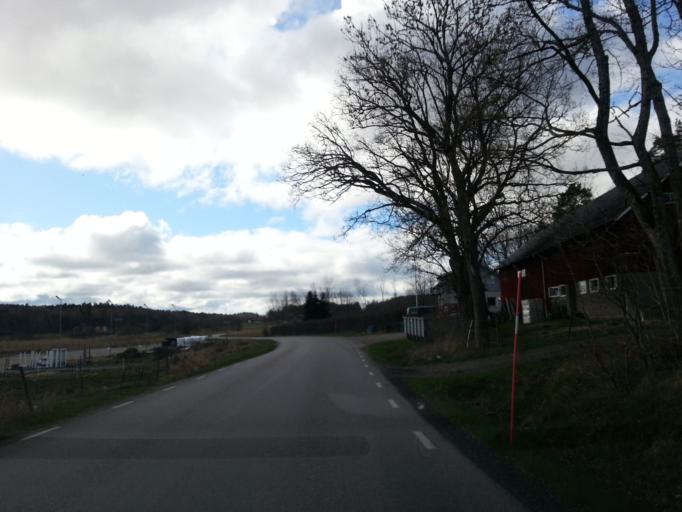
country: SE
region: Vaestra Goetaland
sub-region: Kungalvs Kommun
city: Kode
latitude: 57.8504
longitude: 11.8807
